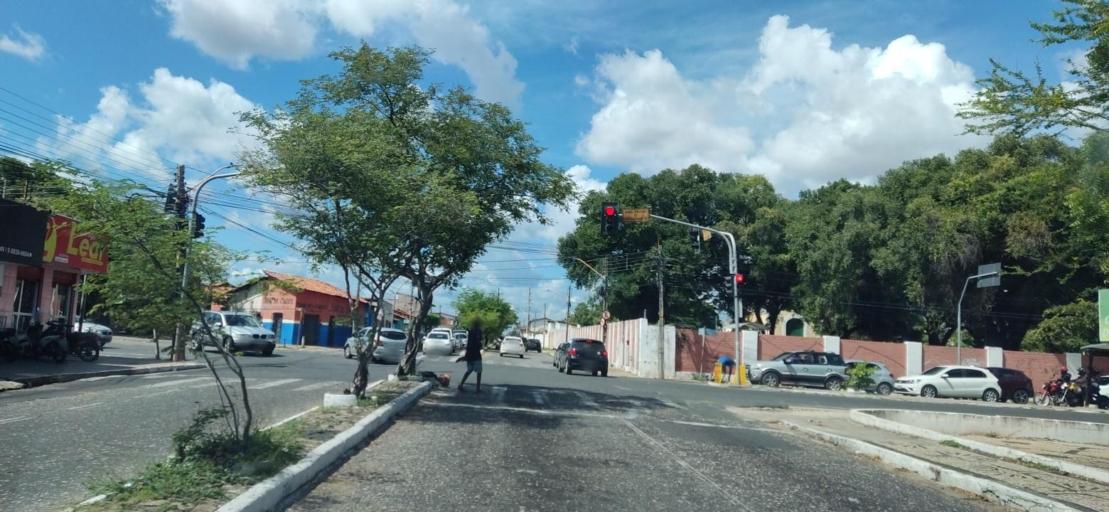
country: BR
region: Maranhao
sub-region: Timon
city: Timon
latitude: -5.0797
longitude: -42.8224
